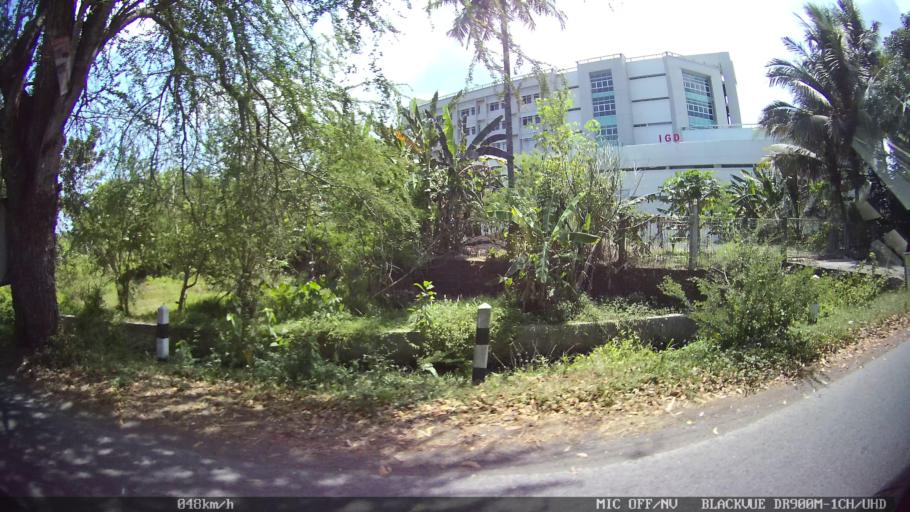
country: ID
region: Daerah Istimewa Yogyakarta
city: Pandak
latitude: -7.9101
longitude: 110.2957
